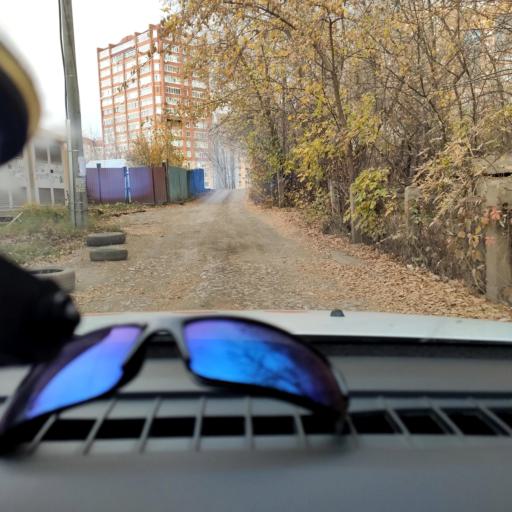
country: RU
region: Samara
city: Samara
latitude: 53.2360
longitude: 50.1780
